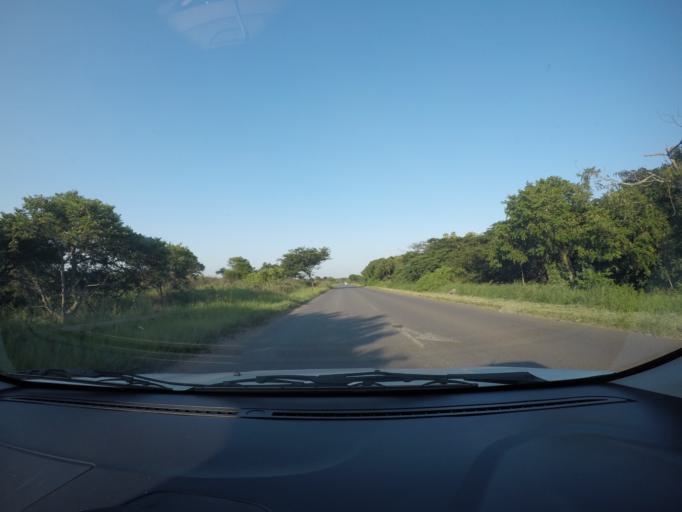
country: ZA
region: KwaZulu-Natal
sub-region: uThungulu District Municipality
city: Richards Bay
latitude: -28.7545
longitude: 32.0070
